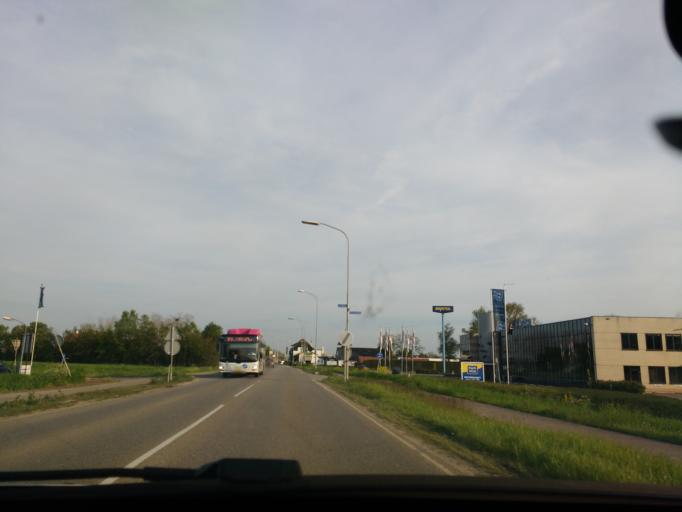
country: NL
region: Gelderland
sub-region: Gemeente Overbetuwe
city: Oosterhout
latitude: 51.8903
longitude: 5.8385
